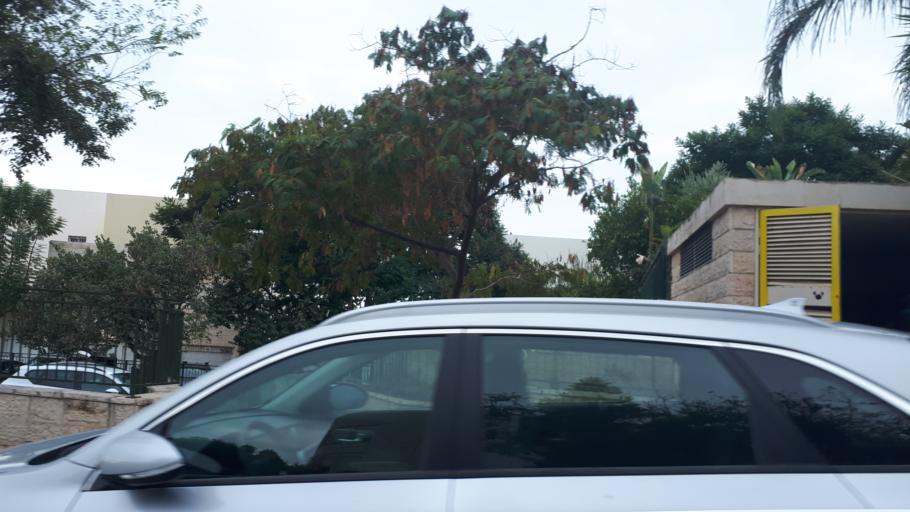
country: IL
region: Central District
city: Modiin
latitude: 31.9042
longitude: 35.0110
